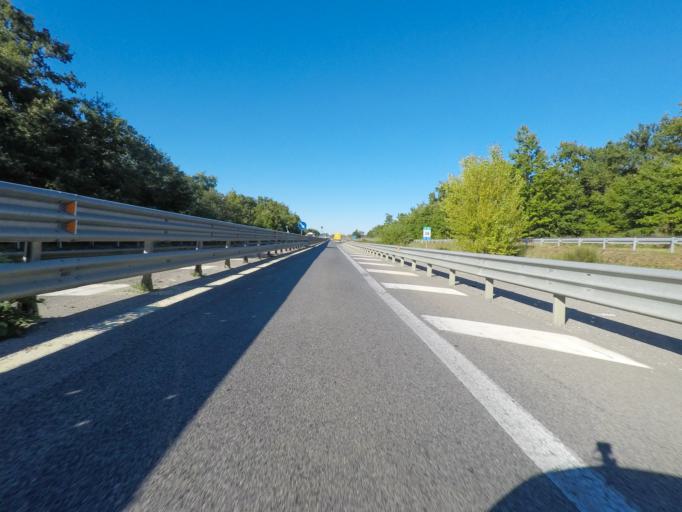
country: IT
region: Tuscany
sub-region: Provincia di Siena
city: Rosia
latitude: 43.2241
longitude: 11.2739
